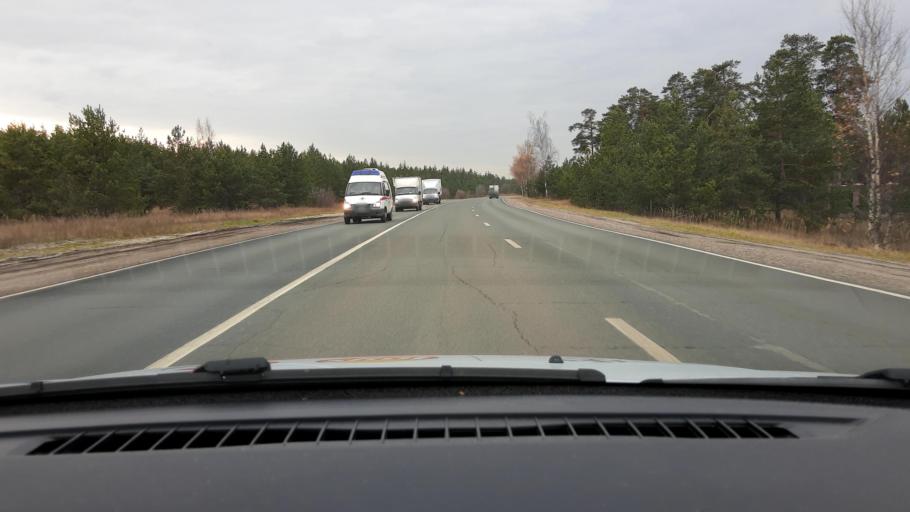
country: RU
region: Nizjnij Novgorod
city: Dzerzhinsk
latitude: 56.2766
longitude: 43.4750
